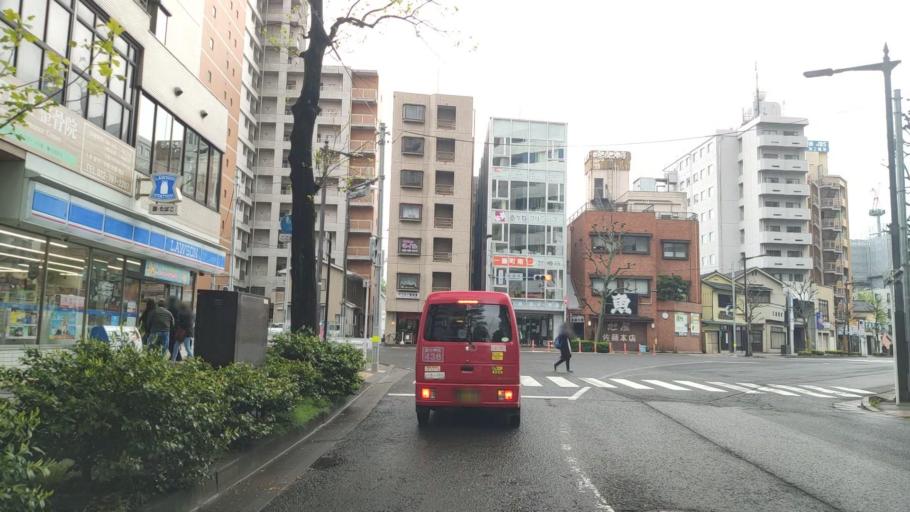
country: JP
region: Miyagi
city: Sendai
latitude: 38.2553
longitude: 140.8765
